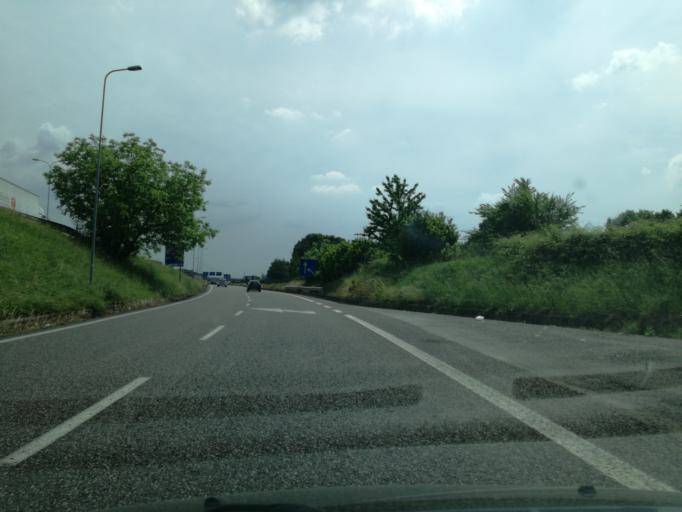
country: IT
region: Lombardy
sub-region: Provincia di Monza e Brianza
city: Giussano
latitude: 45.6844
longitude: 9.2157
